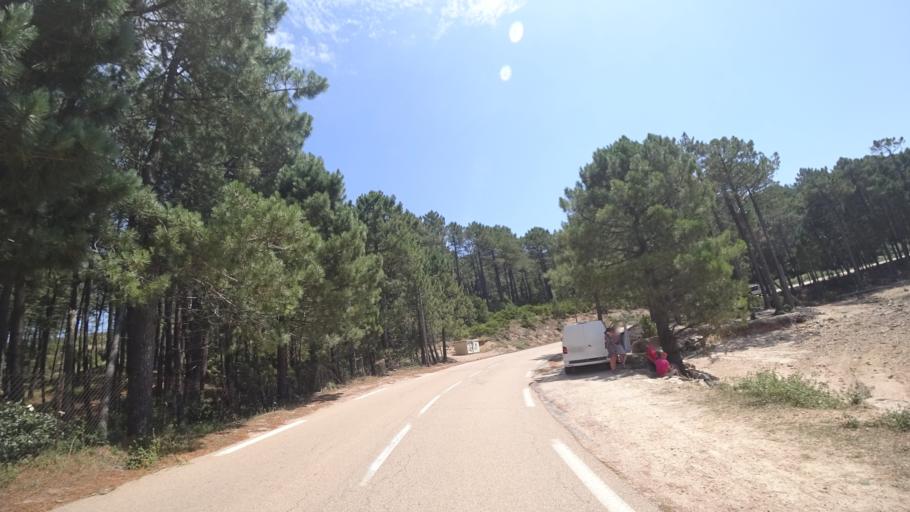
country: FR
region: Corsica
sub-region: Departement de la Corse-du-Sud
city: Zonza
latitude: 41.6680
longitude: 9.2090
